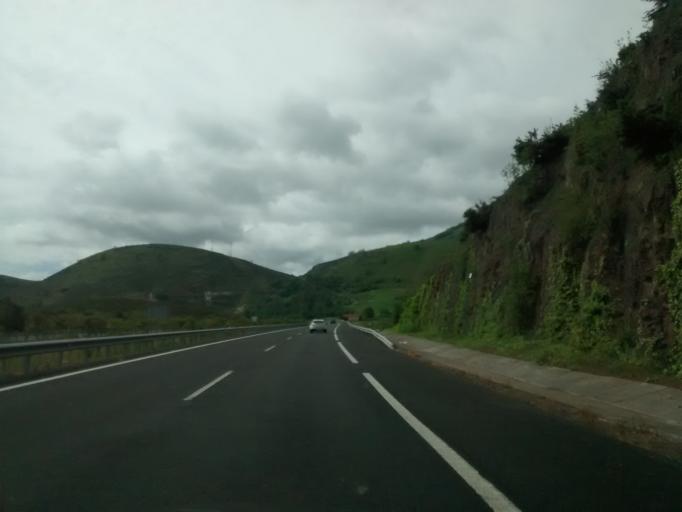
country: ES
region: Cantabria
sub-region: Provincia de Cantabria
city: Los Corrales de Buelna
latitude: 43.2217
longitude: -4.0788
